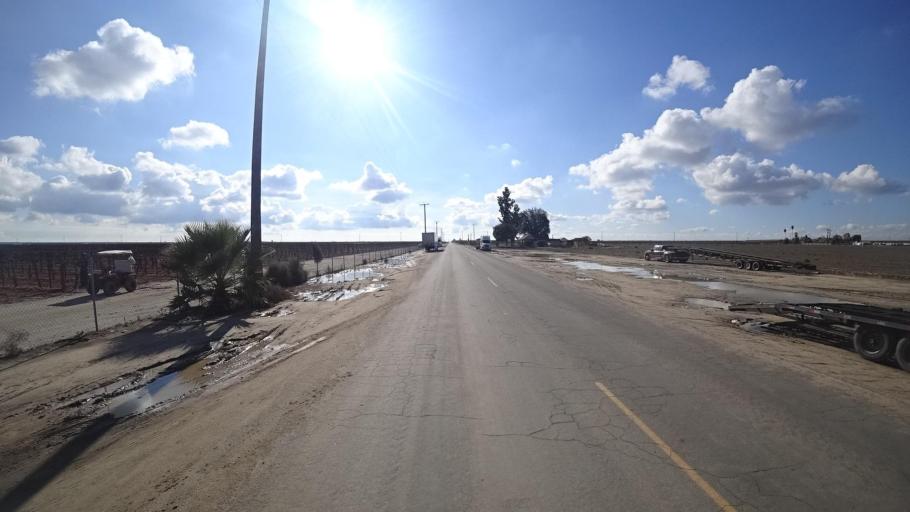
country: US
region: California
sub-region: Kern County
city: McFarland
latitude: 35.6634
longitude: -119.2322
